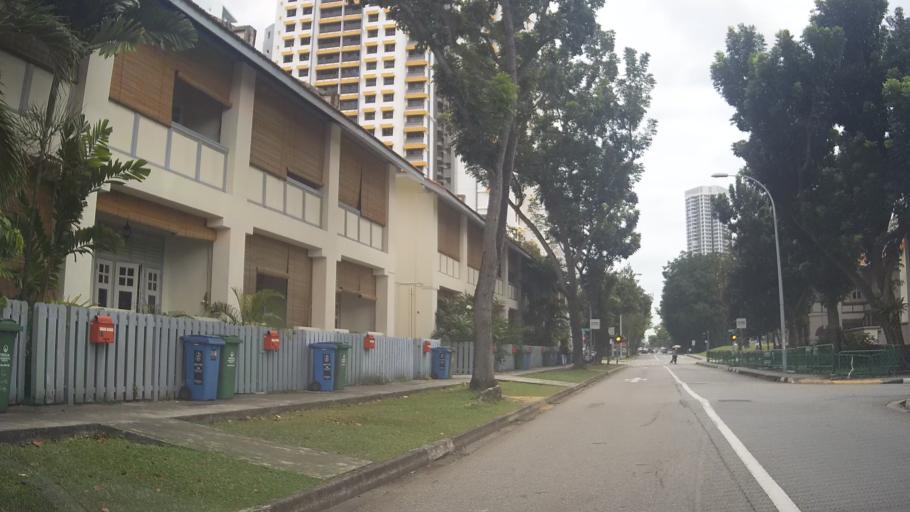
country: SG
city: Singapore
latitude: 1.3209
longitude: 103.8581
